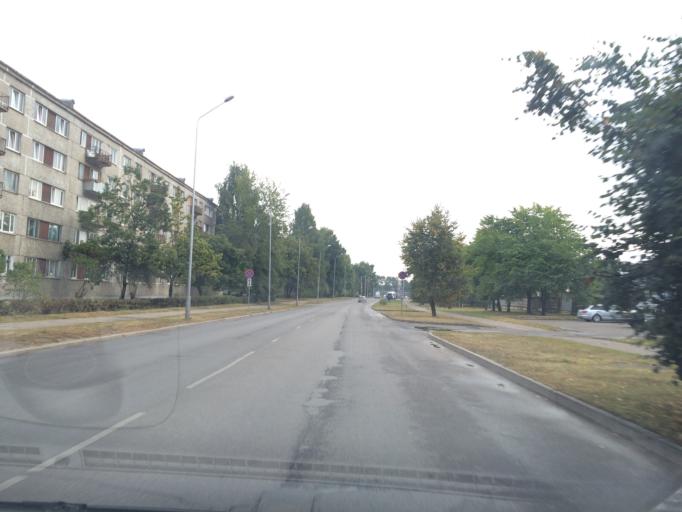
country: LV
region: Kekava
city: Kekava
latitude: 56.8976
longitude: 24.2125
